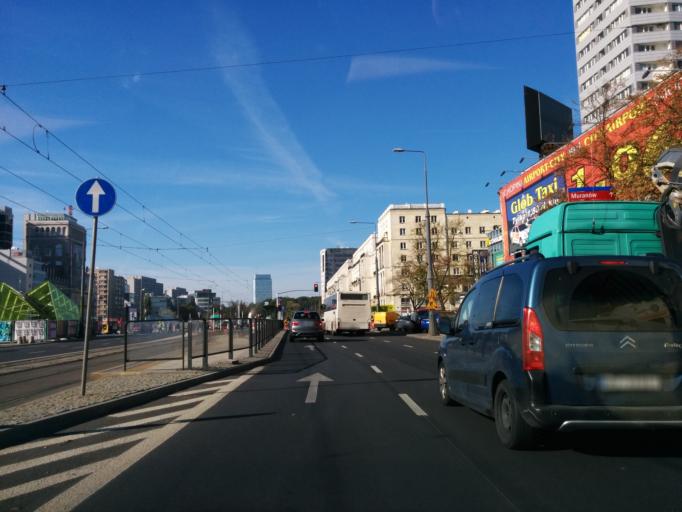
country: PL
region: Masovian Voivodeship
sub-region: Warszawa
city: Warsaw
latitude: 52.2342
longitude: 21.0092
